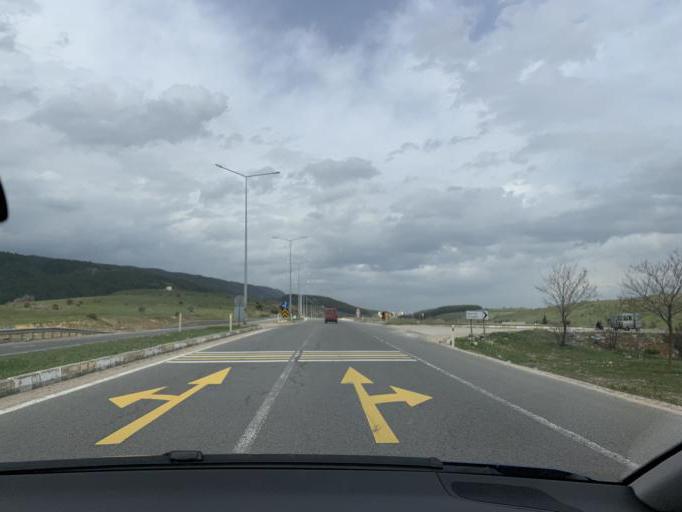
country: TR
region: Bolu
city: Gerede
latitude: 40.7960
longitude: 32.1550
